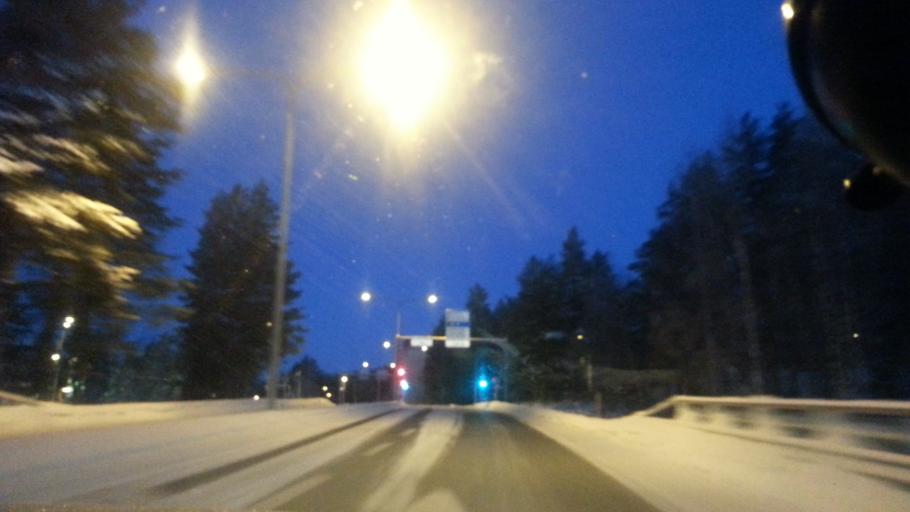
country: FI
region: Lapland
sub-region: Rovaniemi
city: Rovaniemi
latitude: 66.4966
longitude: 25.7570
